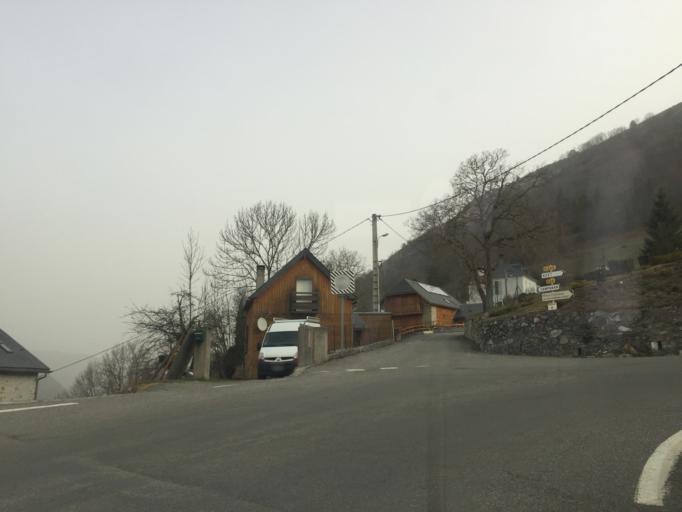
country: FR
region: Midi-Pyrenees
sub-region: Departement des Hautes-Pyrenees
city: Saint-Lary-Soulan
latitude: 42.8187
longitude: 0.3431
